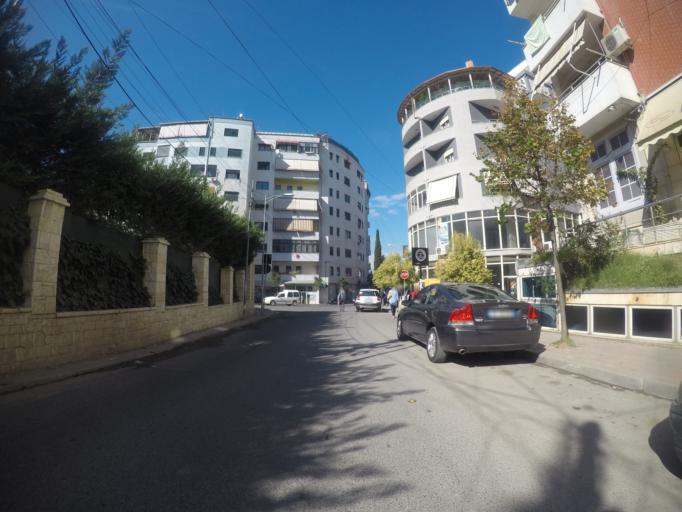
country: AL
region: Tirane
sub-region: Rrethi i Tiranes
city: Farka e Madhe
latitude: 41.3460
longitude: 19.8564
